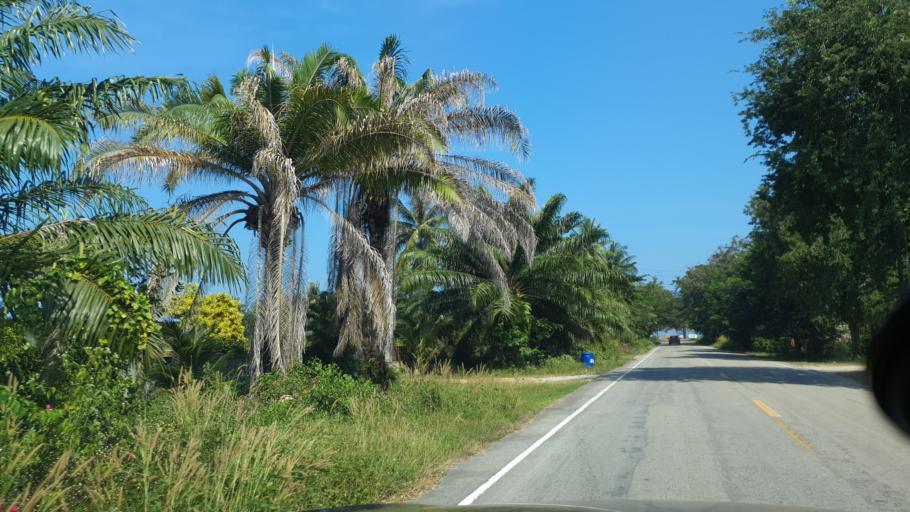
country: TH
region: Surat Thani
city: Tha Chana
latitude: 9.5878
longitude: 99.2051
